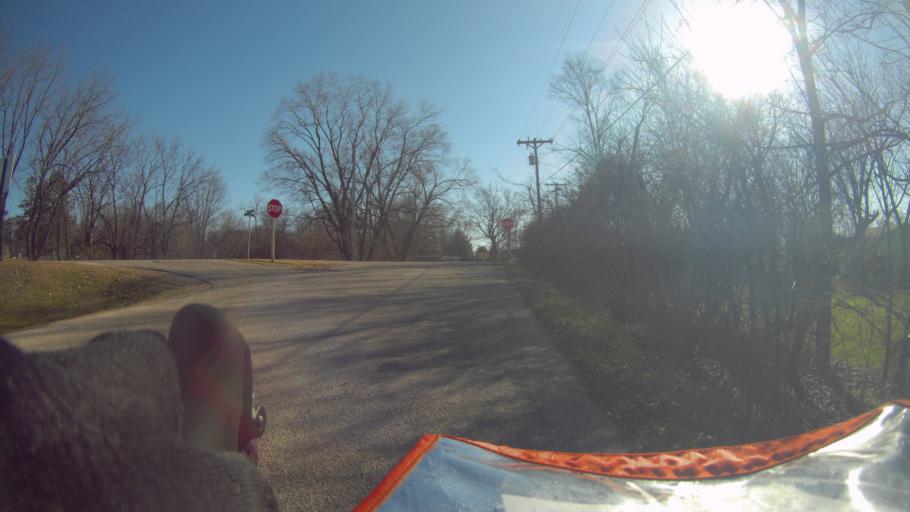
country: US
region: Wisconsin
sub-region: Green County
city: Brooklyn
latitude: 42.8503
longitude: -89.3693
